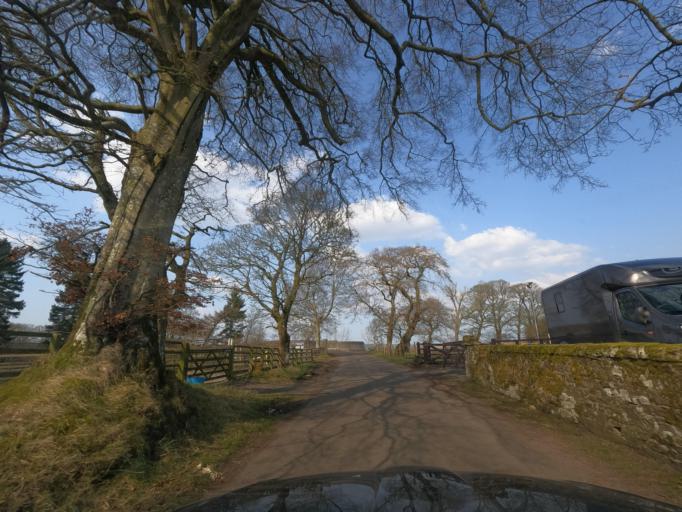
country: GB
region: Scotland
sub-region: South Lanarkshire
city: Carnwath
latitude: 55.7420
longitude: -3.6153
